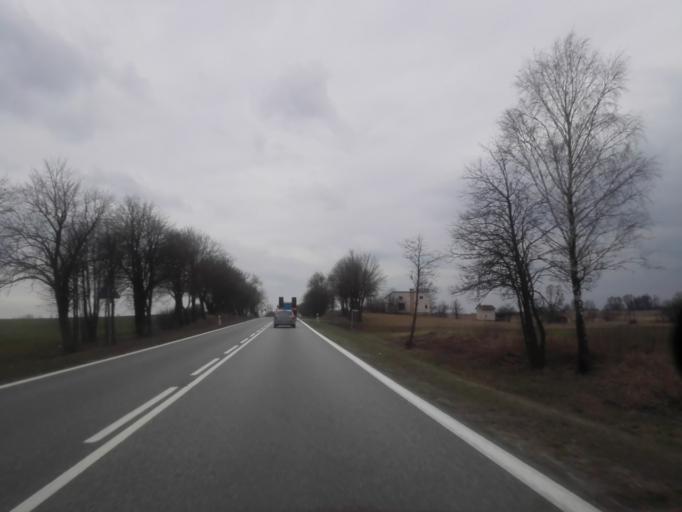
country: PL
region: Podlasie
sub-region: Powiat augustowski
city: Augustow
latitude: 53.8196
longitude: 22.9318
